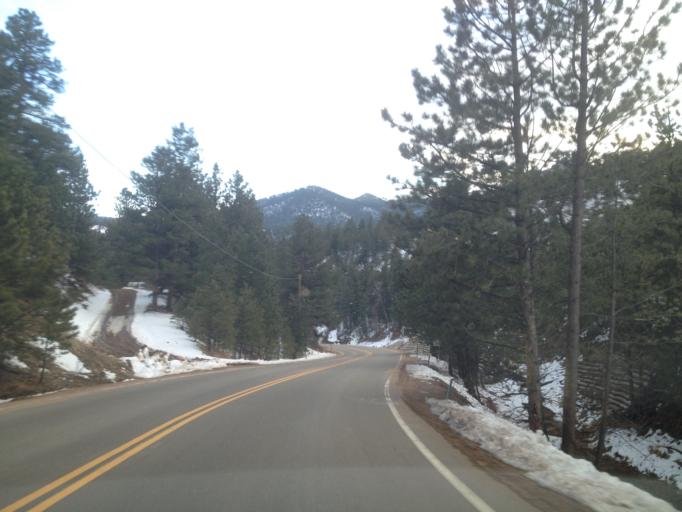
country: US
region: Colorado
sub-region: Boulder County
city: Lyons
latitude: 40.1200
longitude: -105.3940
